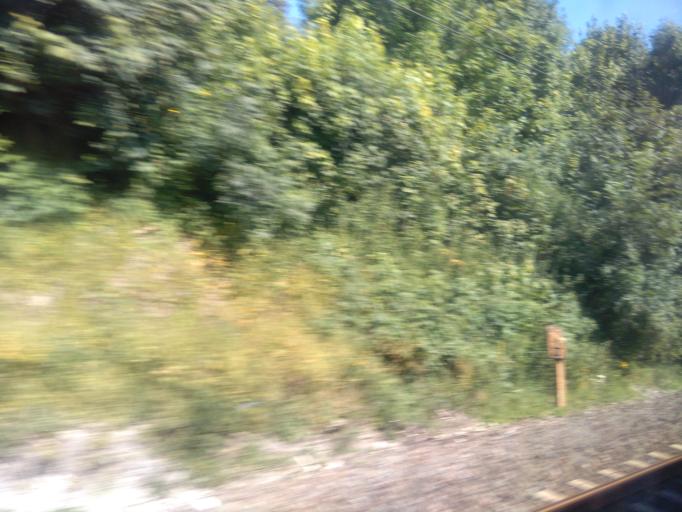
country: GB
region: England
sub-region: Luton
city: Luton
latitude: 51.8613
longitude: -0.3835
